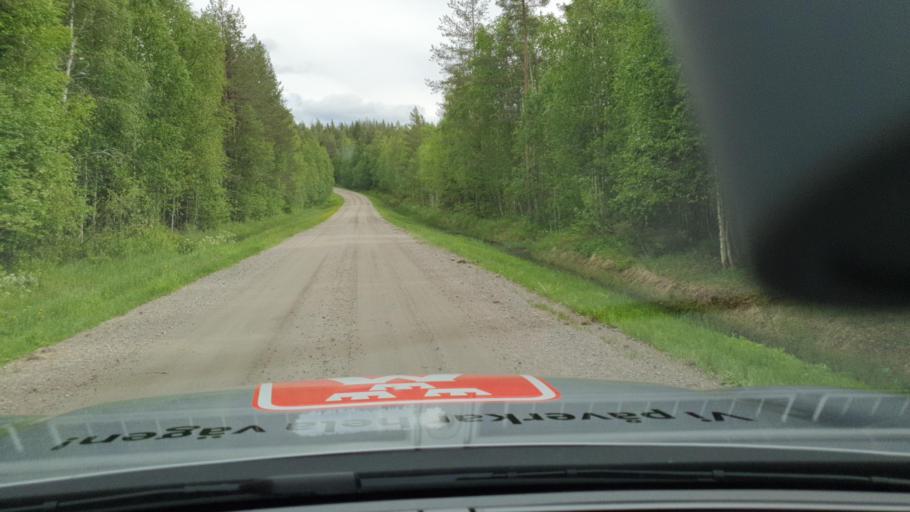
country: FI
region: Lapland
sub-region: Torniolaakso
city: Ylitornio
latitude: 65.9430
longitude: 23.5410
